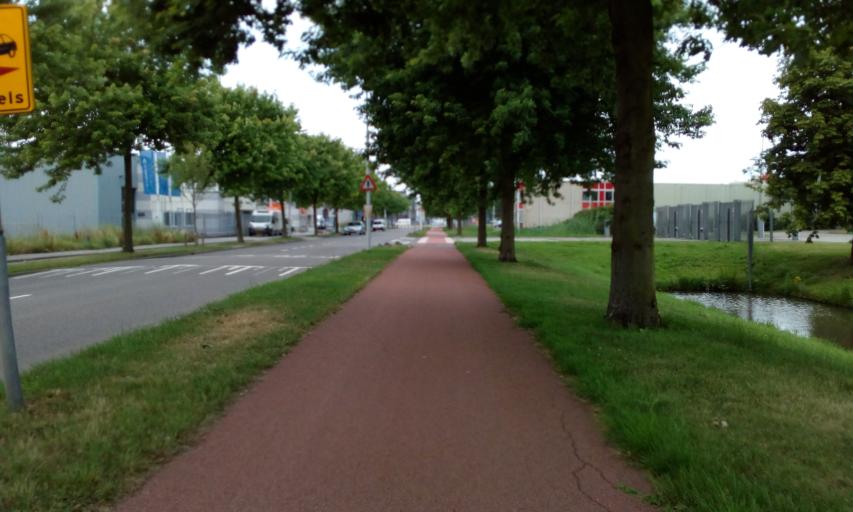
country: NL
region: South Holland
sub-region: Gemeente Rotterdam
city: Delfshaven
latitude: 51.9223
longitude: 4.4320
